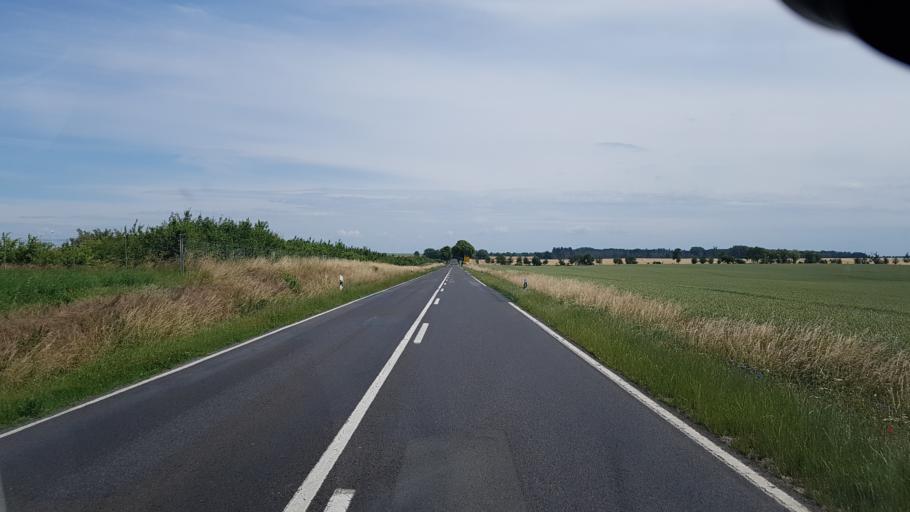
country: DE
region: Mecklenburg-Vorpommern
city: Strasburg
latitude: 53.4025
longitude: 13.7487
